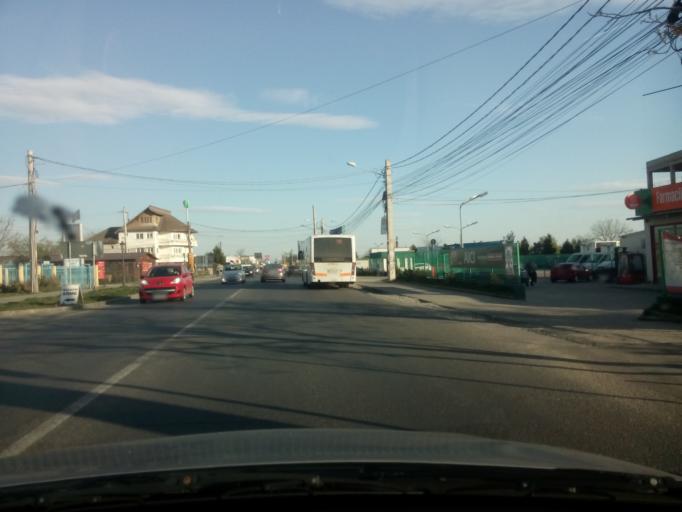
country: RO
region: Ilfov
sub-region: Comuna Mogosoaia
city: Mogosoaia
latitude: 44.5170
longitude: 26.0136
